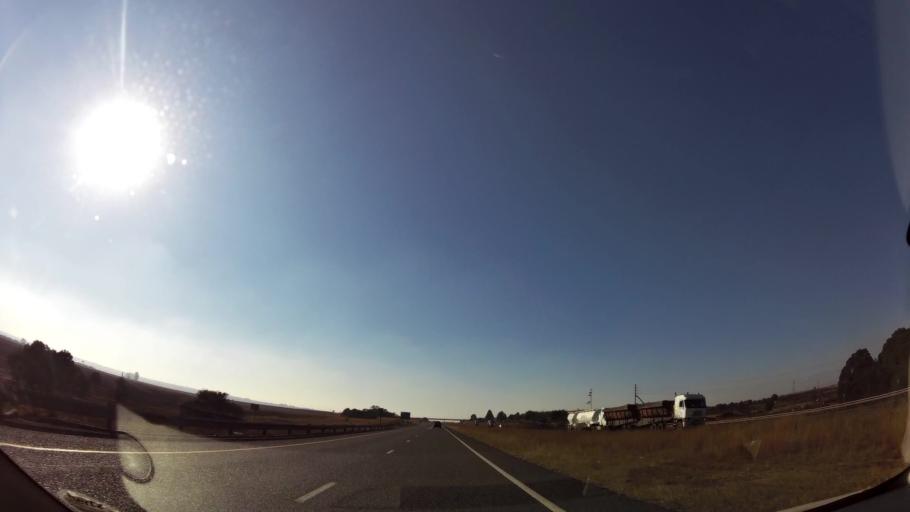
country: ZA
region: Mpumalanga
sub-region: Nkangala District Municipality
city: Witbank
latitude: -26.0214
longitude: 29.0285
